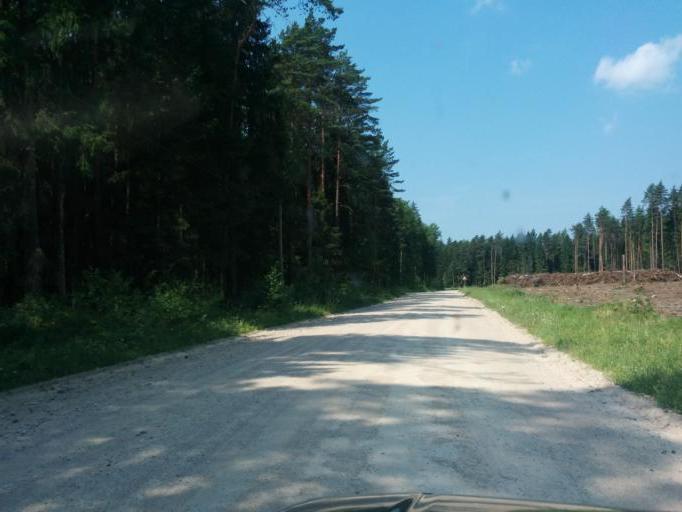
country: LV
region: Baldone
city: Baldone
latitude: 56.7472
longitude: 24.4570
